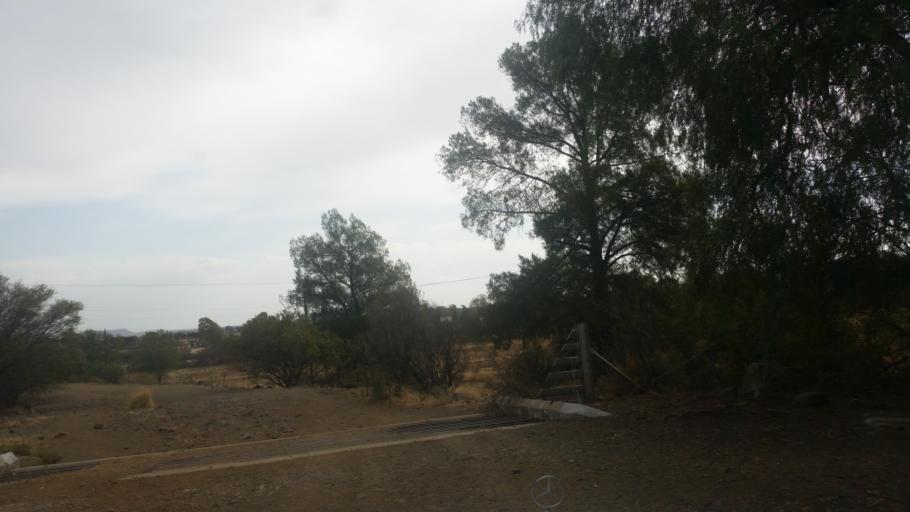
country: ZA
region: Orange Free State
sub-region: Xhariep District Municipality
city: Trompsburg
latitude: -30.4915
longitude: 25.9979
